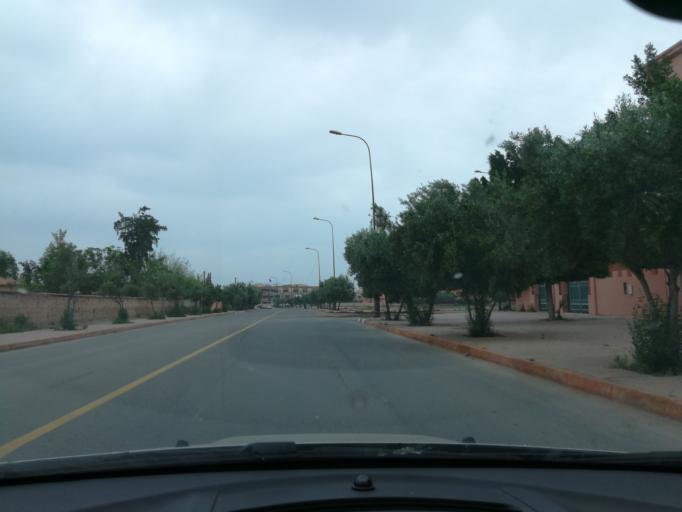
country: MA
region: Marrakech-Tensift-Al Haouz
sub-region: Marrakech
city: Marrakesh
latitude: 31.6758
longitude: -7.9997
